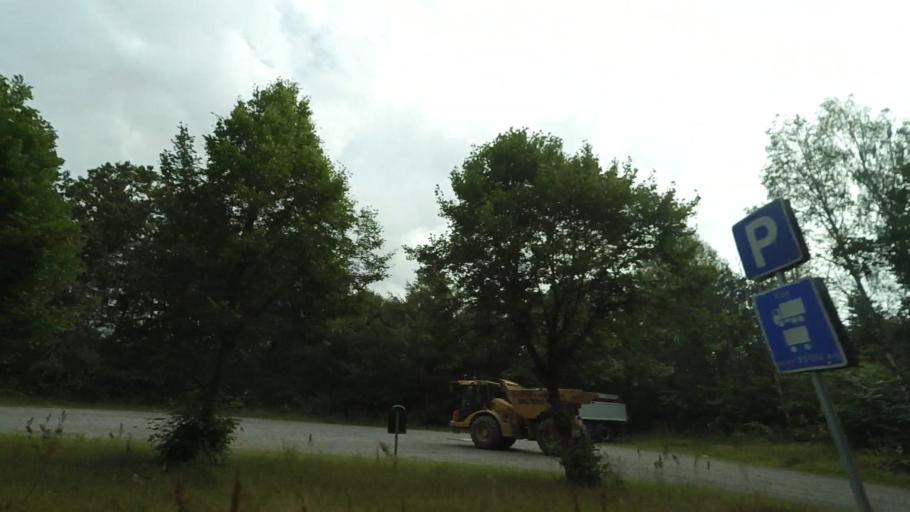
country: DK
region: Central Jutland
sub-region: Syddjurs Kommune
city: Ryomgard
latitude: 56.4161
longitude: 10.5611
